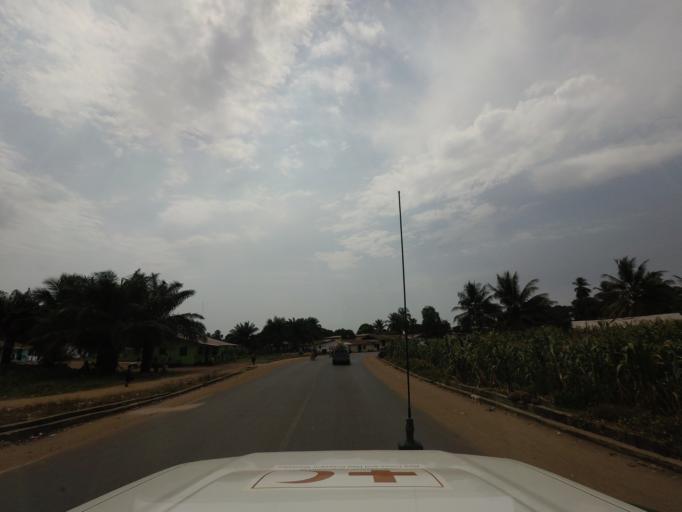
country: LR
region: Montserrado
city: Monrovia
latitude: 6.2902
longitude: -10.6794
